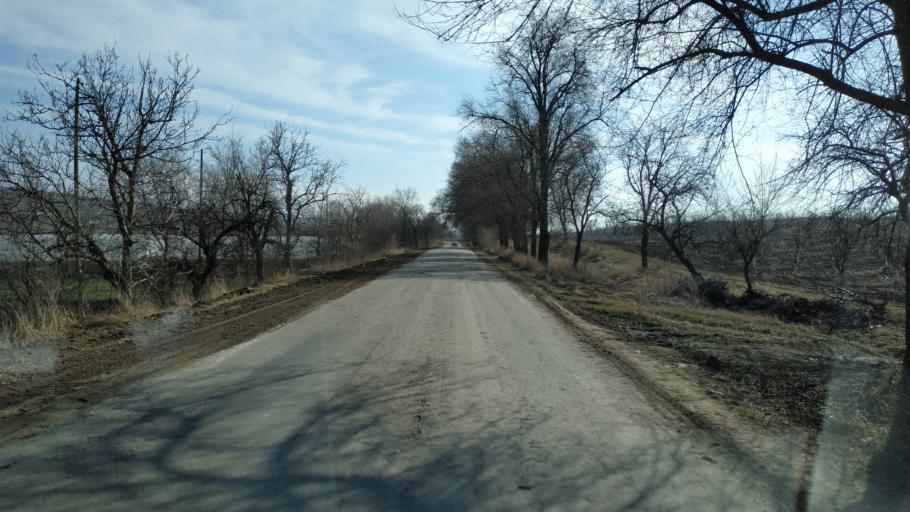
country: MD
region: Nisporeni
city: Nisporeni
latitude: 47.0818
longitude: 28.1438
